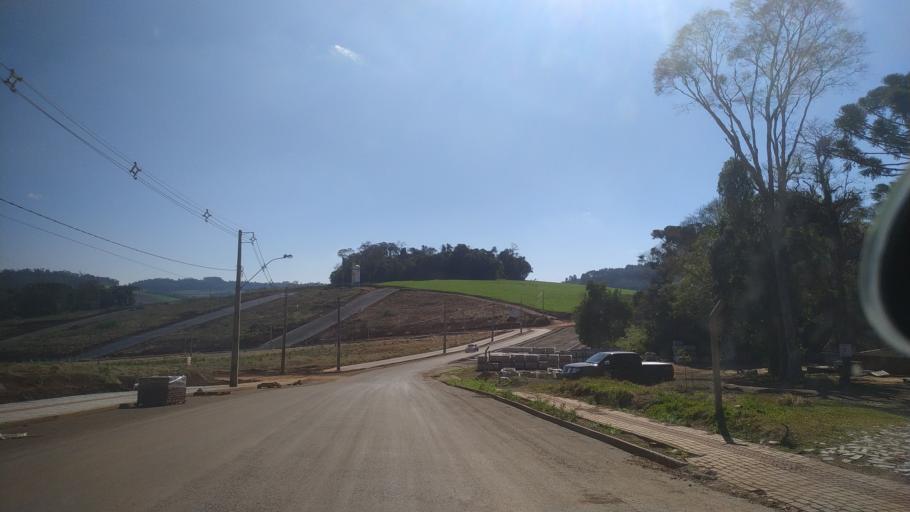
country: BR
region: Santa Catarina
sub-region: Chapeco
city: Chapeco
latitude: -27.0867
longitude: -52.6920
